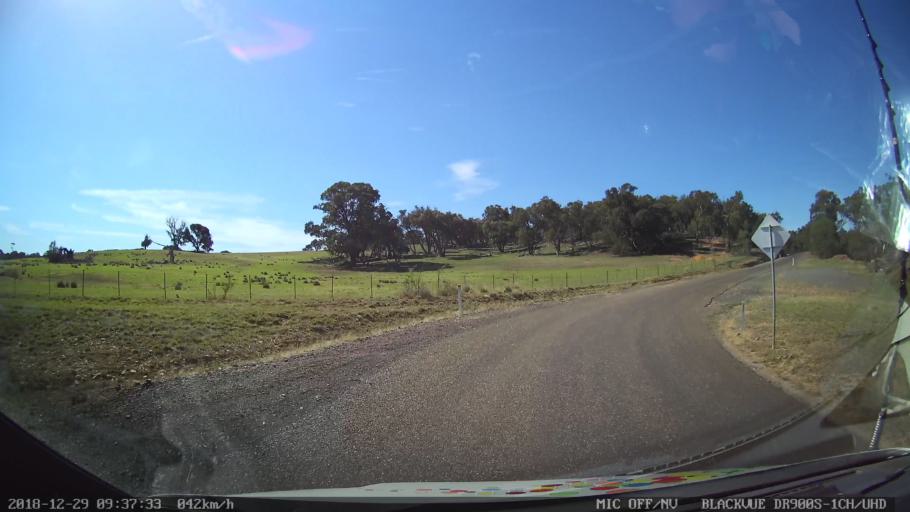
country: AU
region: New South Wales
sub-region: Upper Lachlan Shire
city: Crookwell
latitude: -34.6396
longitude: 149.3748
